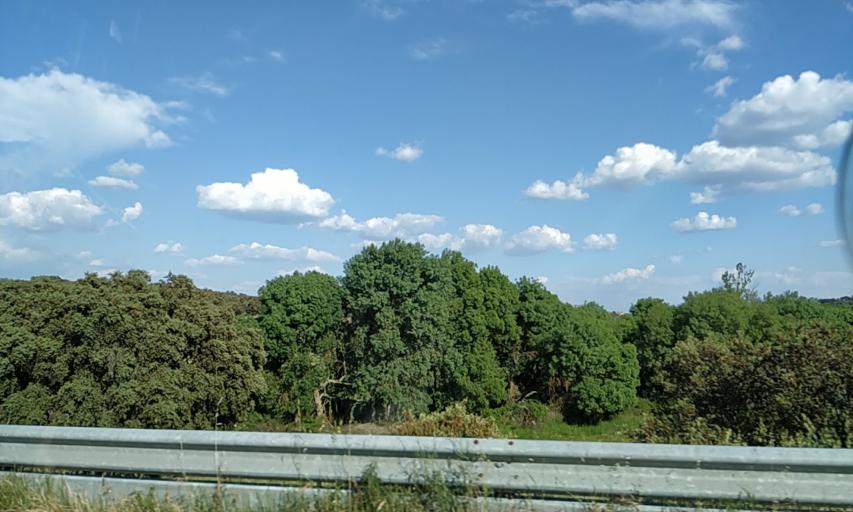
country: PT
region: Portalegre
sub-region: Fronteira
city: Fronteira
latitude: 38.9953
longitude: -7.4720
